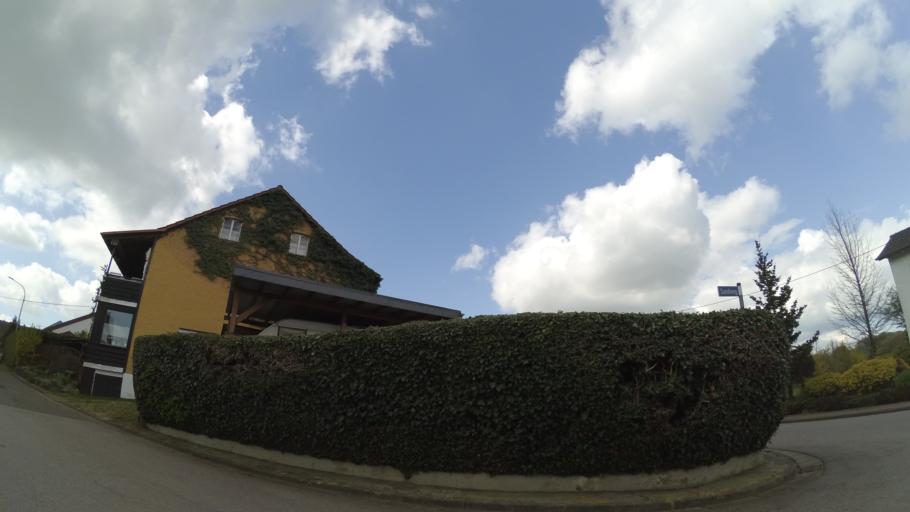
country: DE
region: Saarland
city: Wadern
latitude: 49.5069
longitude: 6.8649
